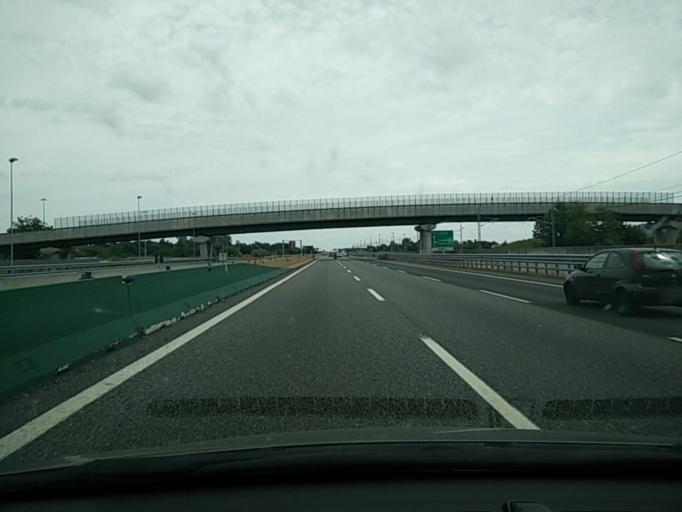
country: IT
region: Piedmont
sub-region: Provincia di Torino
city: Settimo Torinese
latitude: 45.1623
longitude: 7.7896
